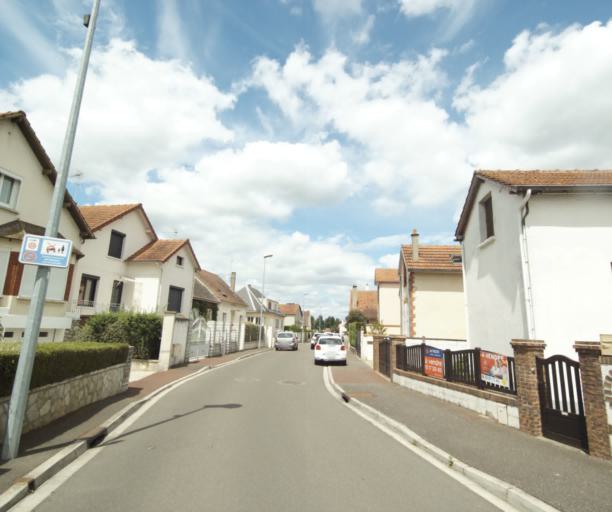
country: FR
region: Centre
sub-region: Departement d'Eure-et-Loir
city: Luce
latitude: 48.4416
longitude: 1.4645
